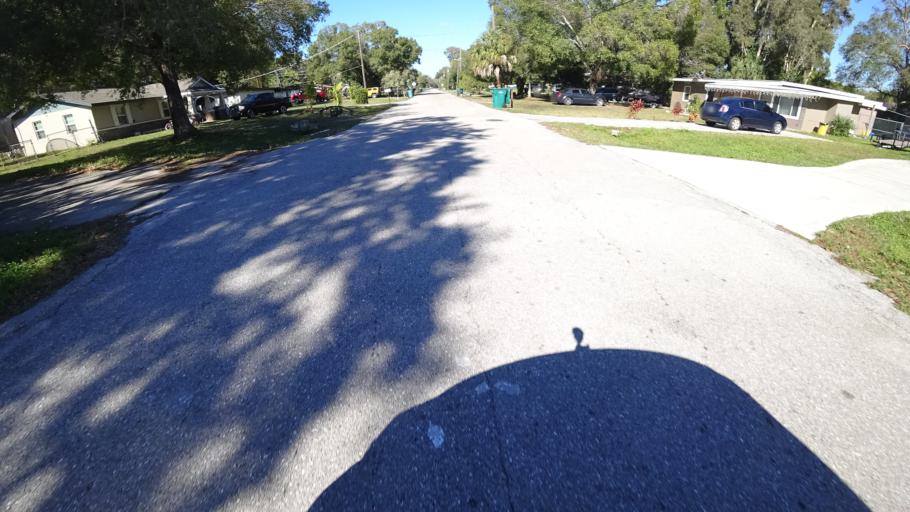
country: US
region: Florida
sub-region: Manatee County
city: Whitfield
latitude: 27.4357
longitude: -82.5493
